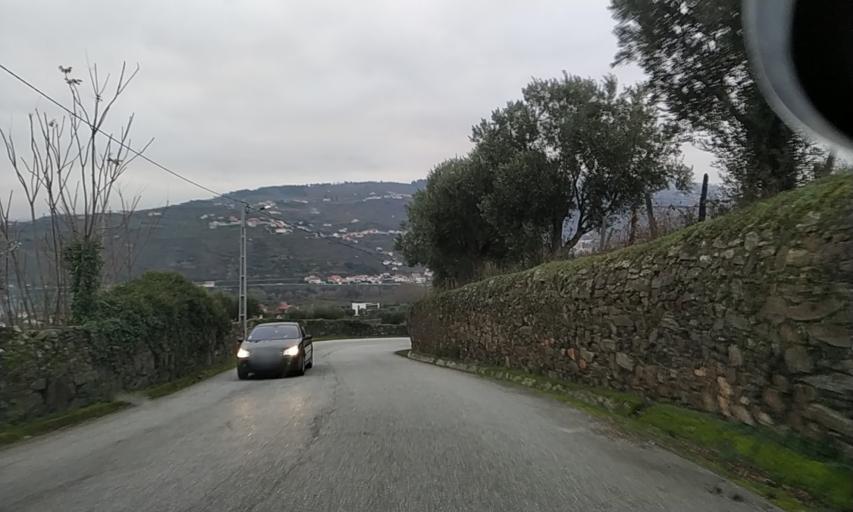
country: PT
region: Vila Real
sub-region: Peso da Regua
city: Peso da Regua
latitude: 41.1506
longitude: -7.7930
